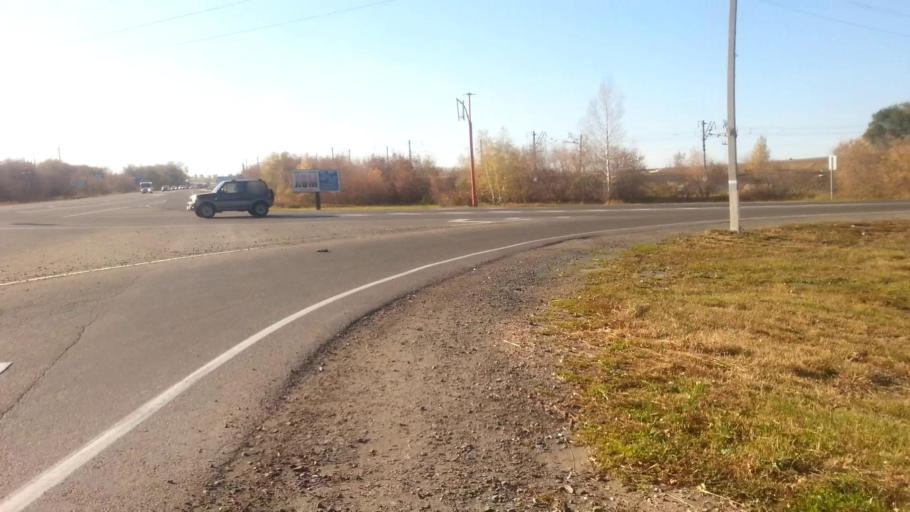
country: RU
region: Altai Krai
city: Novoaltaysk
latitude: 53.3744
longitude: 83.9350
